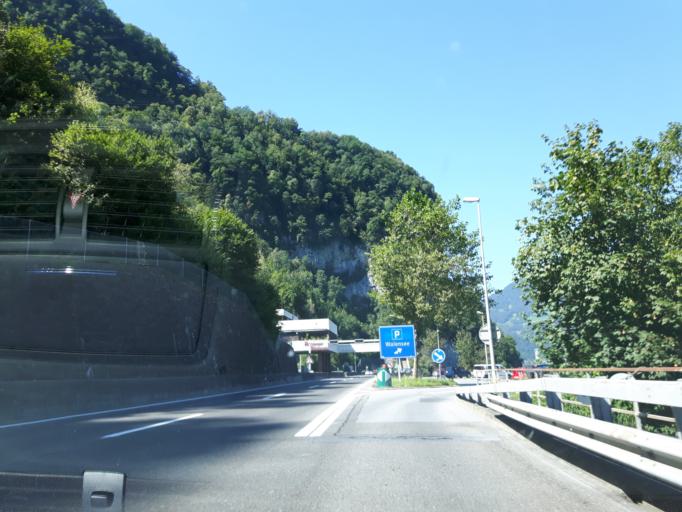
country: CH
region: Saint Gallen
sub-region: Wahlkreis See-Gaster
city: Amden
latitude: 47.1227
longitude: 9.1469
